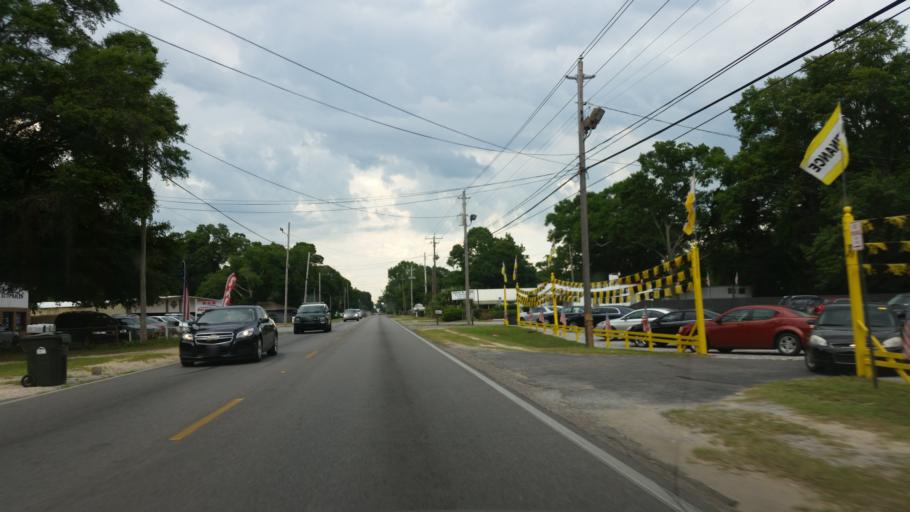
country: US
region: Florida
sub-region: Escambia County
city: Brent
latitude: 30.4902
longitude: -87.2514
